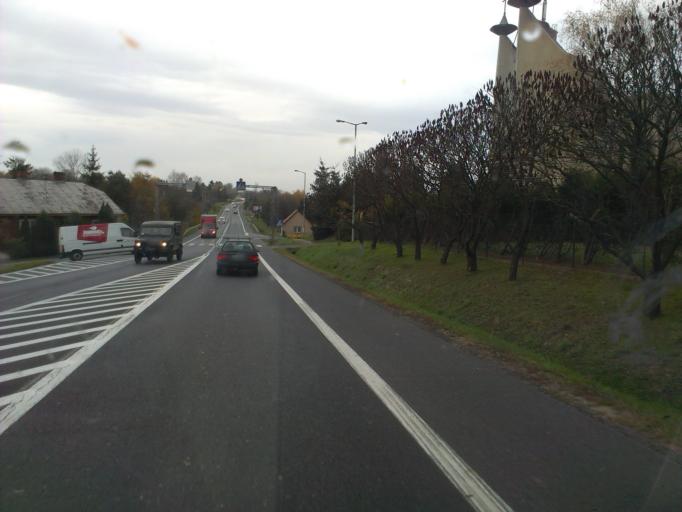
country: PL
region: Subcarpathian Voivodeship
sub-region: Powiat przeworski
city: Mirocin
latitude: 50.0418
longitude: 22.5571
